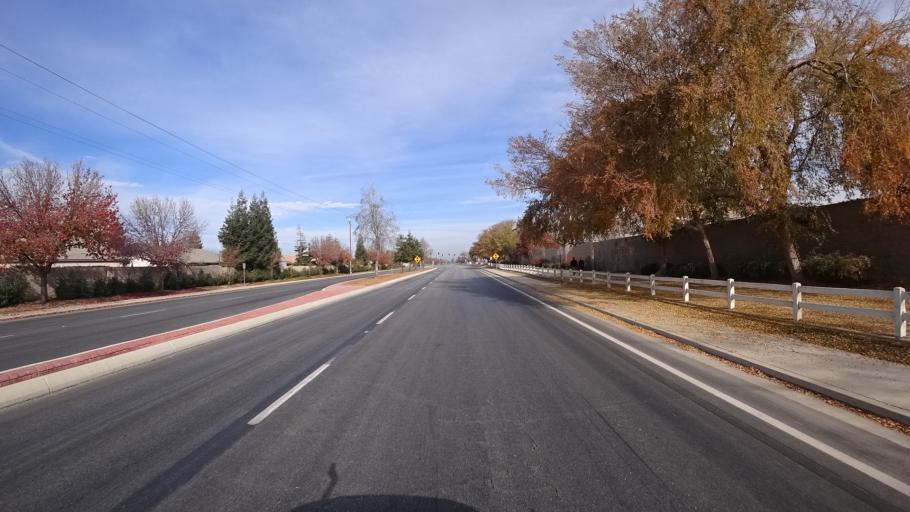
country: US
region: California
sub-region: Kern County
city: Rosedale
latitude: 35.4104
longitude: -119.1277
